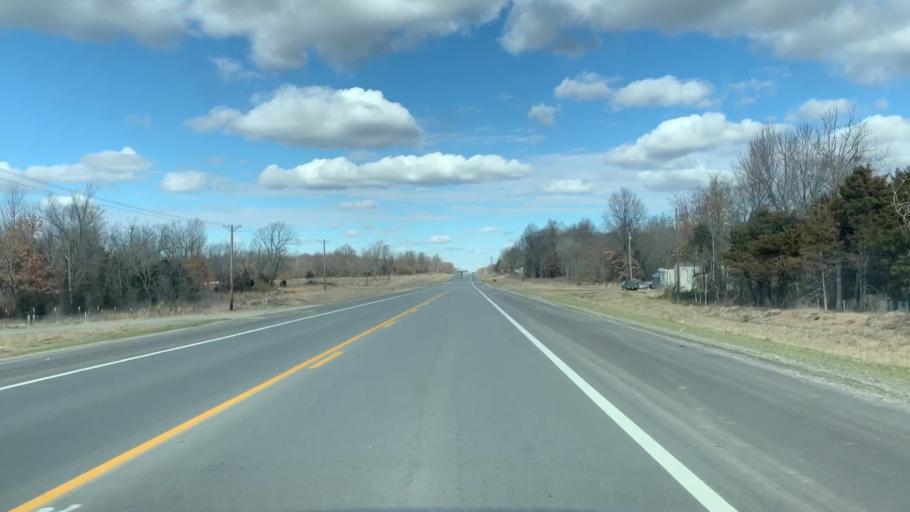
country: US
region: Kansas
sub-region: Cherokee County
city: Columbus
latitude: 37.2243
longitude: -94.8319
